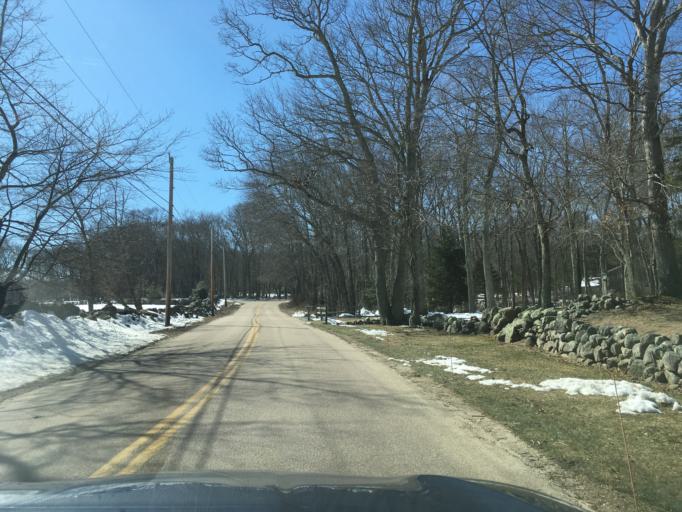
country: US
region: Rhode Island
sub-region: Washington County
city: Exeter
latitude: 41.6039
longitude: -71.5269
